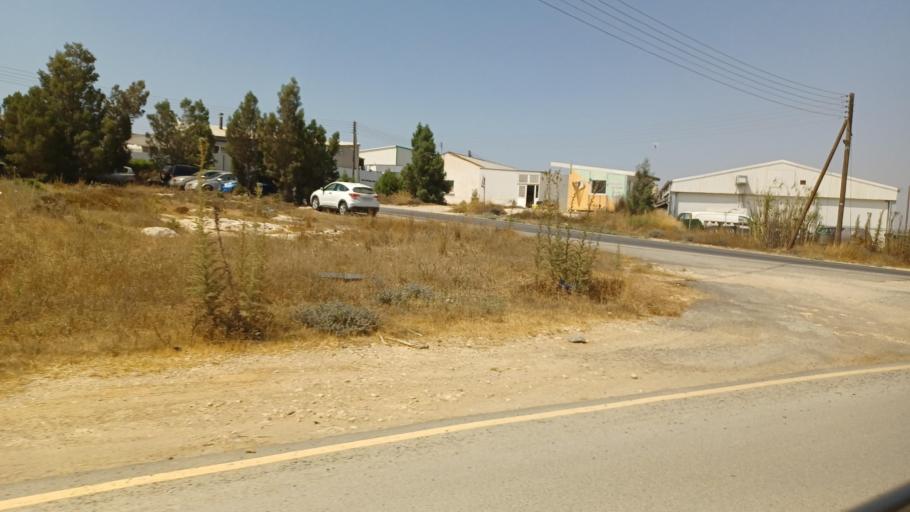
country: CY
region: Ammochostos
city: Deryneia
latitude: 35.0533
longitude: 33.9654
